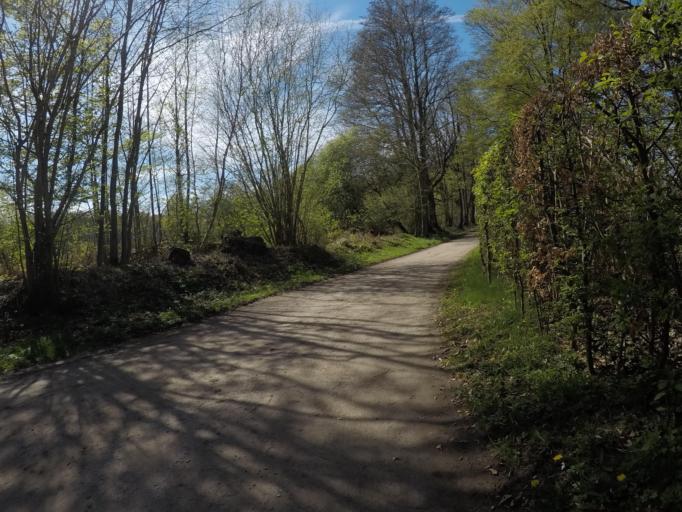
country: DE
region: Schleswig-Holstein
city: Jersbek
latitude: 53.7244
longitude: 10.1780
